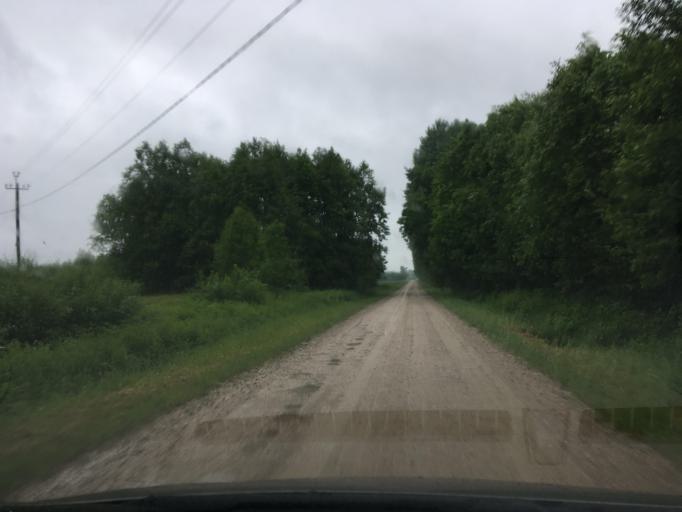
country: EE
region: Laeaene
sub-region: Lihula vald
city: Lihula
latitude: 58.6291
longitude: 23.8150
